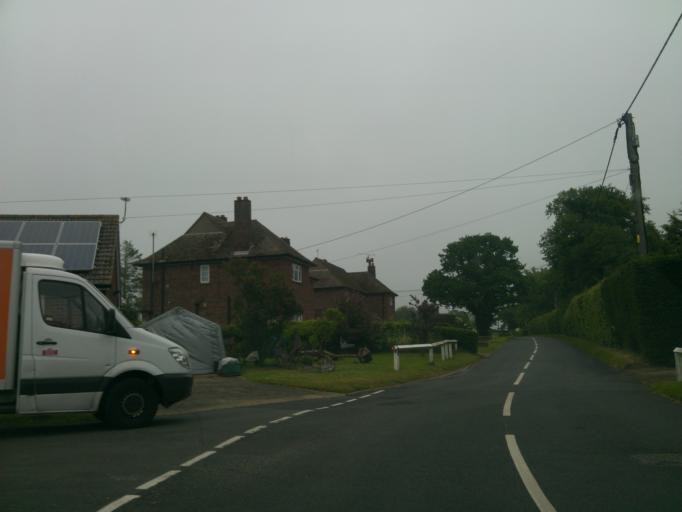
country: GB
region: England
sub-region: Essex
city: Marks Tey
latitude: 51.8509
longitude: 0.8036
